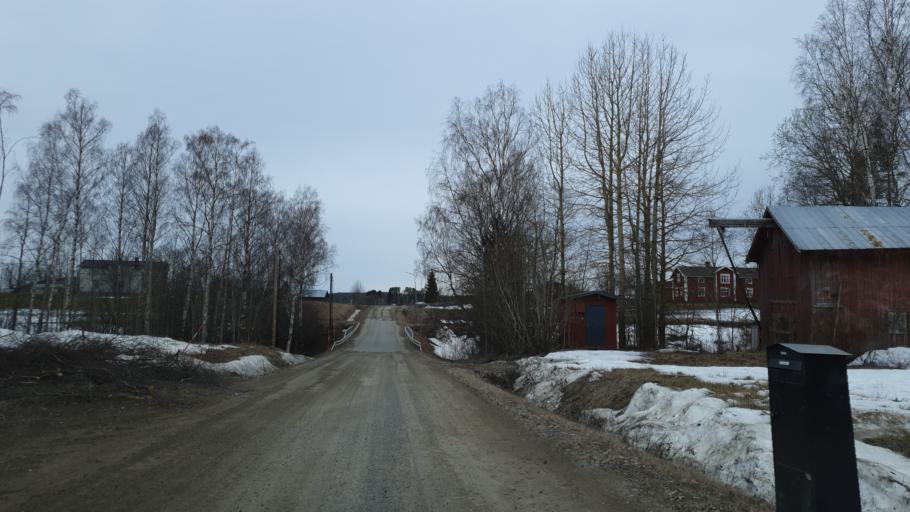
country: SE
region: Vaesterbotten
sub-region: Robertsfors Kommun
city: Robertsfors
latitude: 64.3817
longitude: 20.9179
